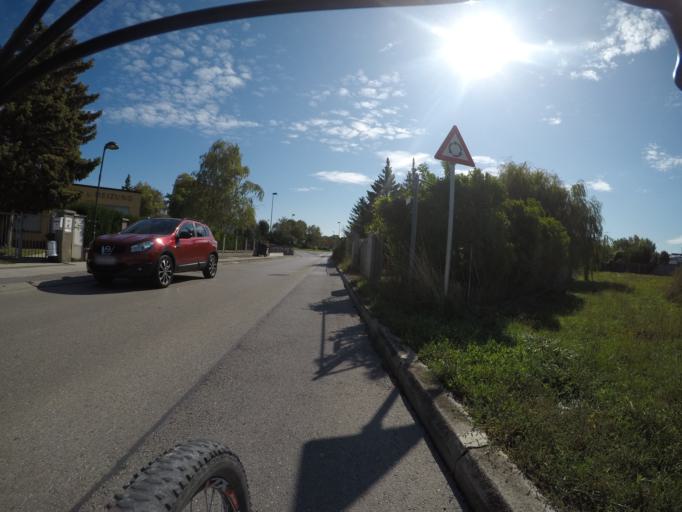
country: AT
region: Lower Austria
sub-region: Politischer Bezirk Modling
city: Maria Enzersdorf
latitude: 48.0983
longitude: 16.2931
